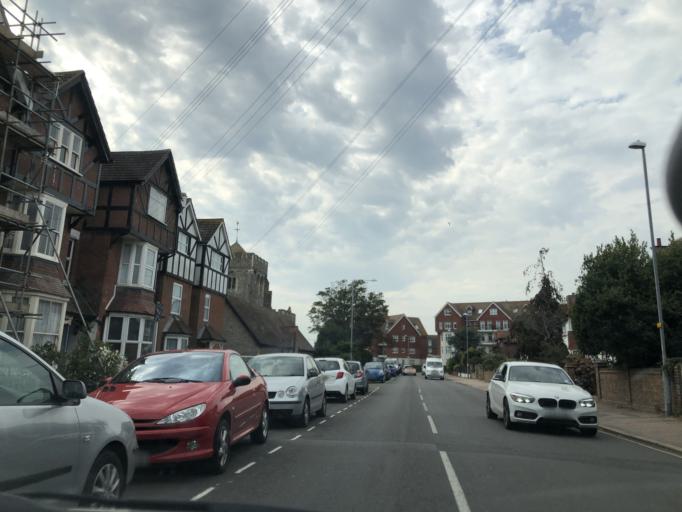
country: GB
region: England
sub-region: East Sussex
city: Bexhill-on-Sea
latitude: 50.8418
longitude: 0.4794
